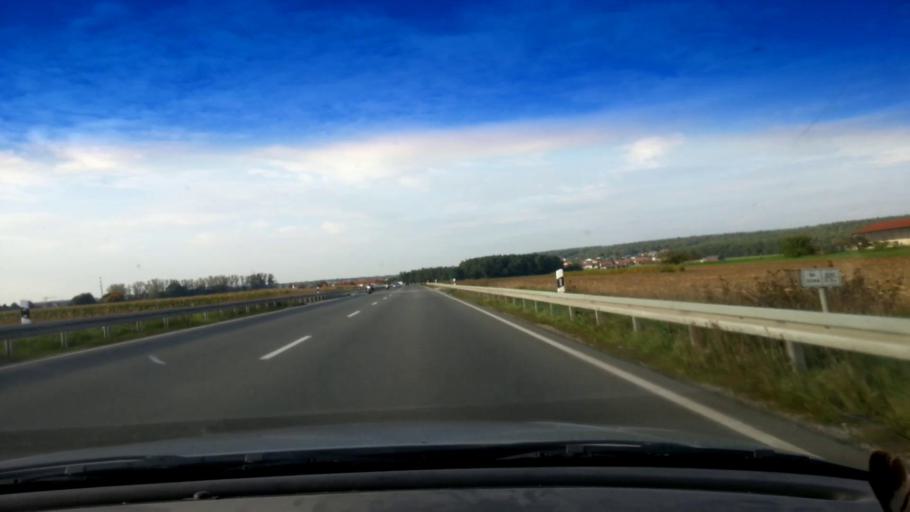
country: DE
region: Bavaria
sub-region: Upper Franconia
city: Strullendorf
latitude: 49.8338
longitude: 10.9778
